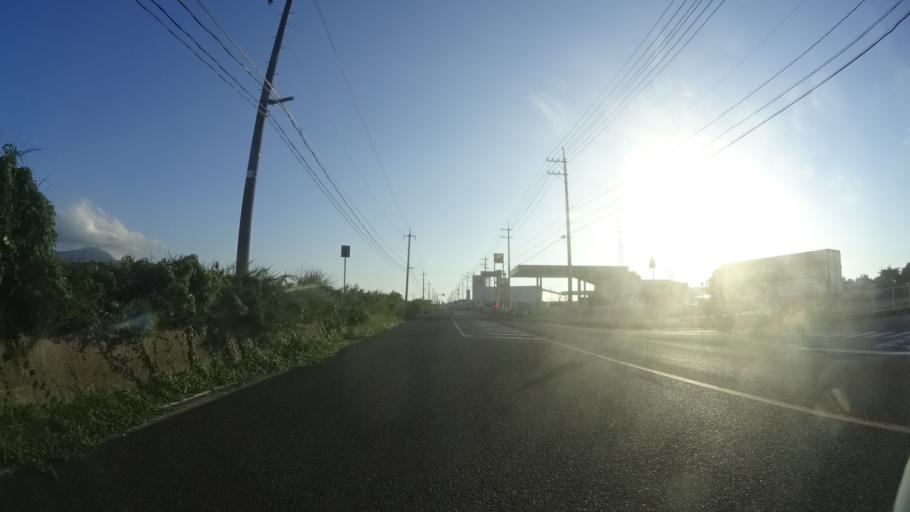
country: JP
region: Tottori
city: Yonago
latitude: 35.5038
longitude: 133.4861
